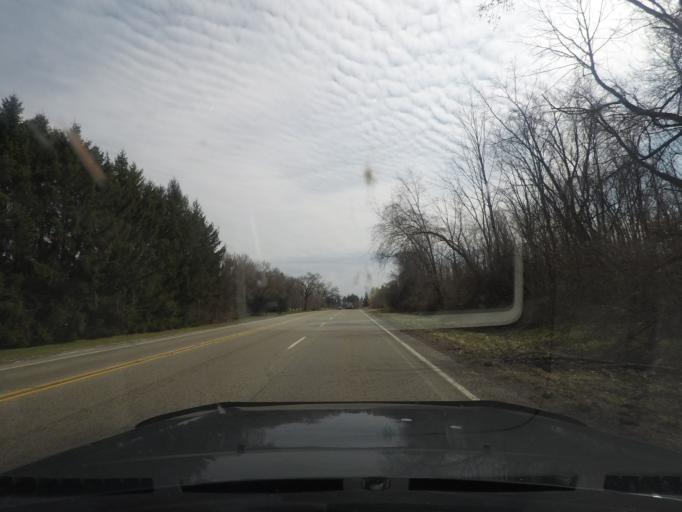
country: US
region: Indiana
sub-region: LaPorte County
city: LaPorte
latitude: 41.6602
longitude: -86.7688
